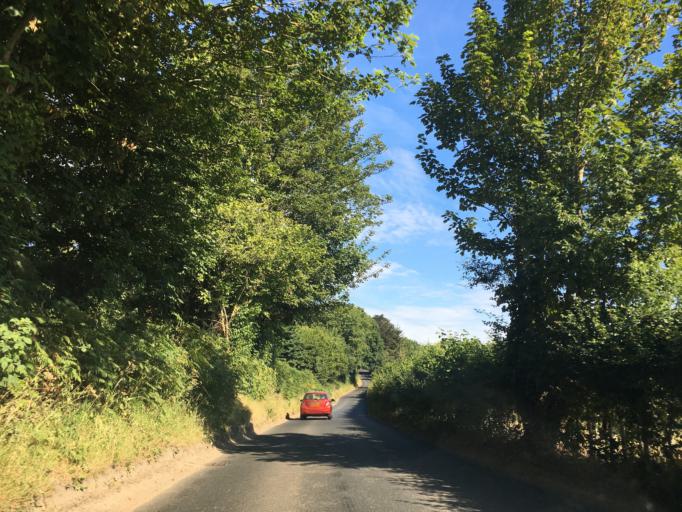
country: GB
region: England
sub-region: Isle of Wight
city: Newport
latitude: 50.6807
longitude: -1.3096
